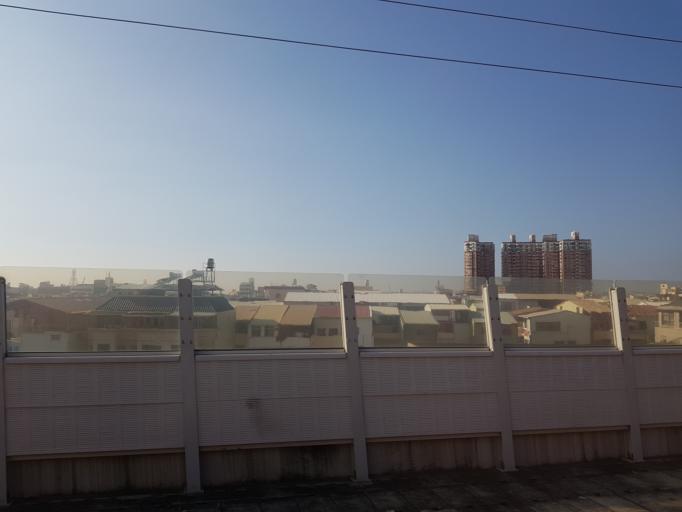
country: TW
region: Taiwan
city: Fengyuan
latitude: 24.2571
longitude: 120.7252
